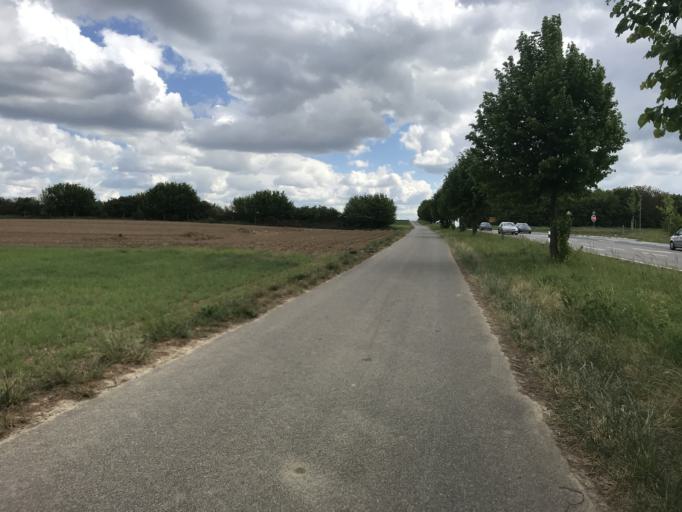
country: DE
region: Rheinland-Pfalz
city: Gau-Bischofsheim
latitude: 49.9229
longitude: 8.2665
